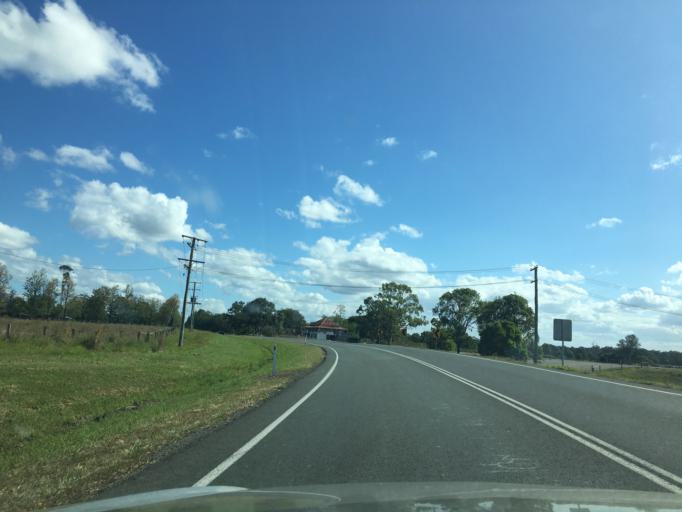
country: AU
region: Queensland
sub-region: Logan
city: Waterford West
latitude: -27.7086
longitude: 153.1325
